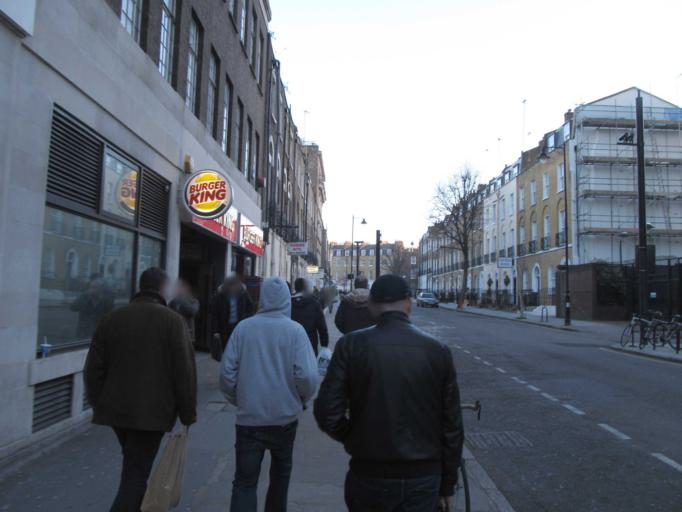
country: GB
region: England
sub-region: Greater London
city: Barnsbury
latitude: 51.5297
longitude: -0.1239
